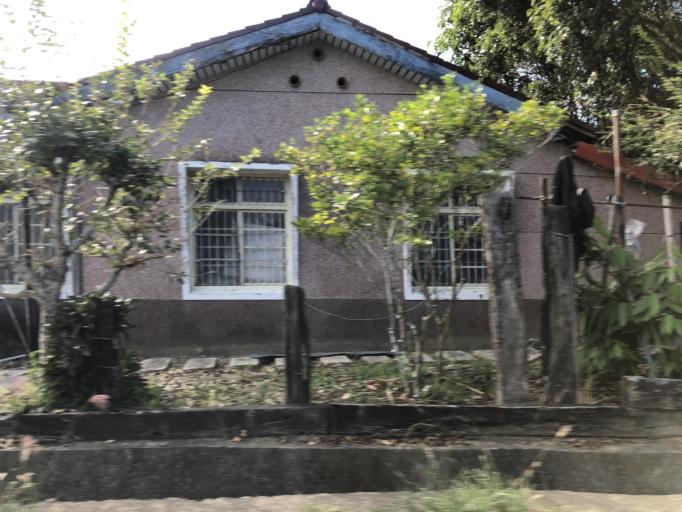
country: TW
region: Taiwan
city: Yujing
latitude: 23.0475
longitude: 120.4010
